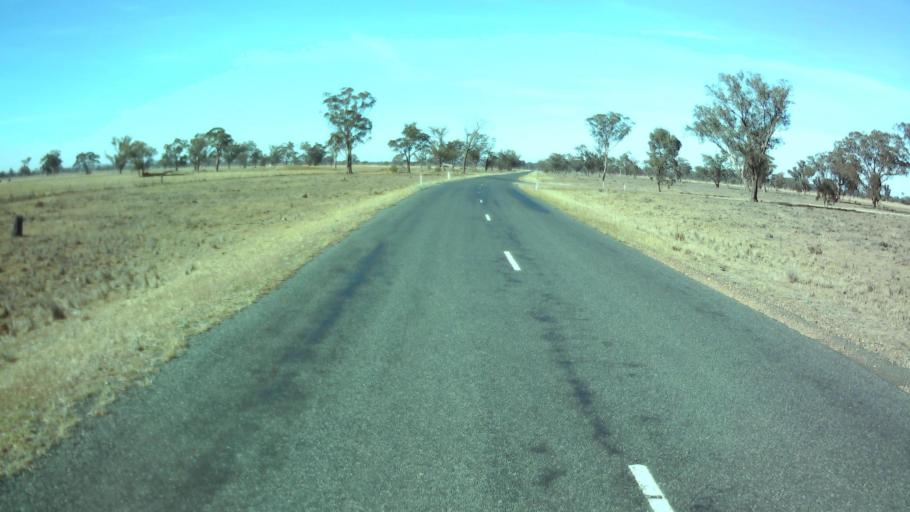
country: AU
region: New South Wales
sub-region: Weddin
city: Grenfell
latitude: -34.0693
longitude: 147.9049
